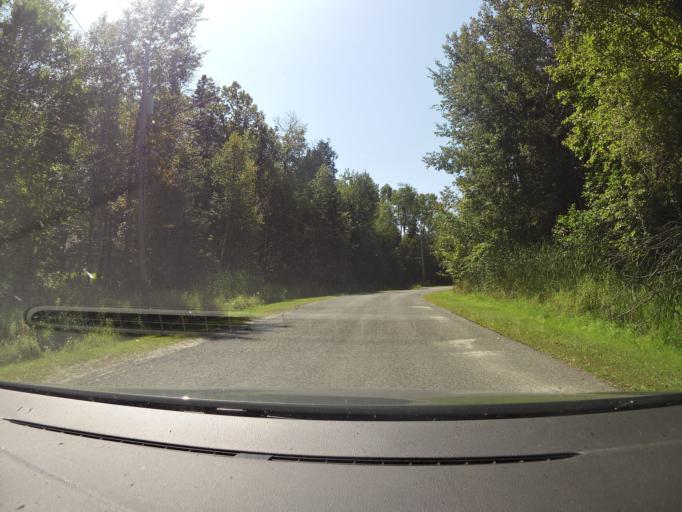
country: CA
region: Ontario
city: Bells Corners
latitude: 45.2805
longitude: -76.0209
